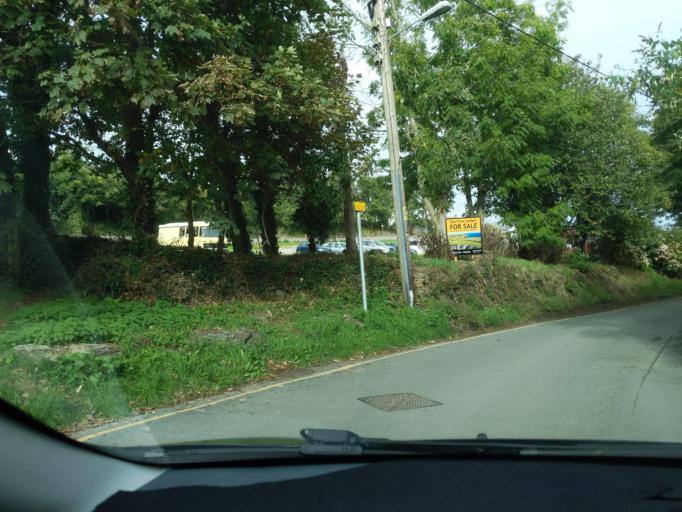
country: GB
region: England
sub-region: Cornwall
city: Mevagissey
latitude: 50.2399
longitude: -4.7918
